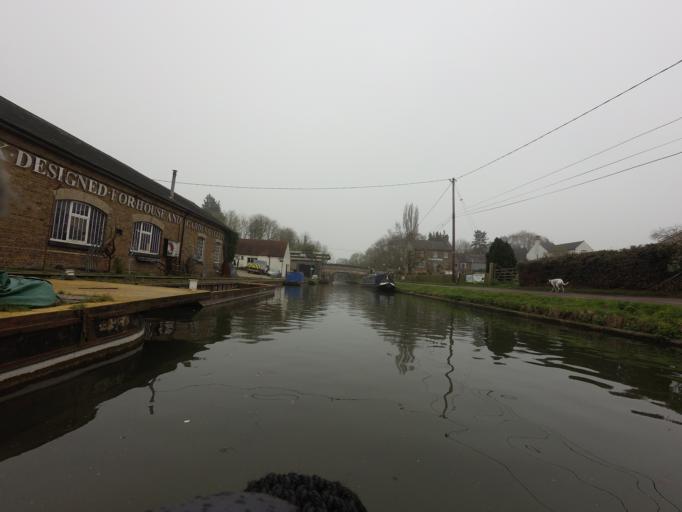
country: GB
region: England
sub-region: Hertfordshire
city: Tring
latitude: 51.8142
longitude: -0.6485
